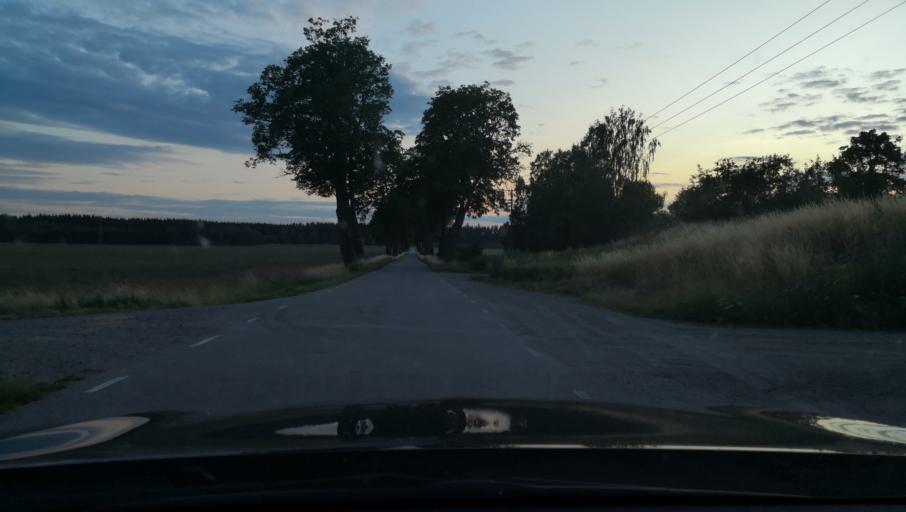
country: SE
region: Uppsala
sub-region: Osthammars Kommun
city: Bjorklinge
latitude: 60.0617
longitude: 17.5616
